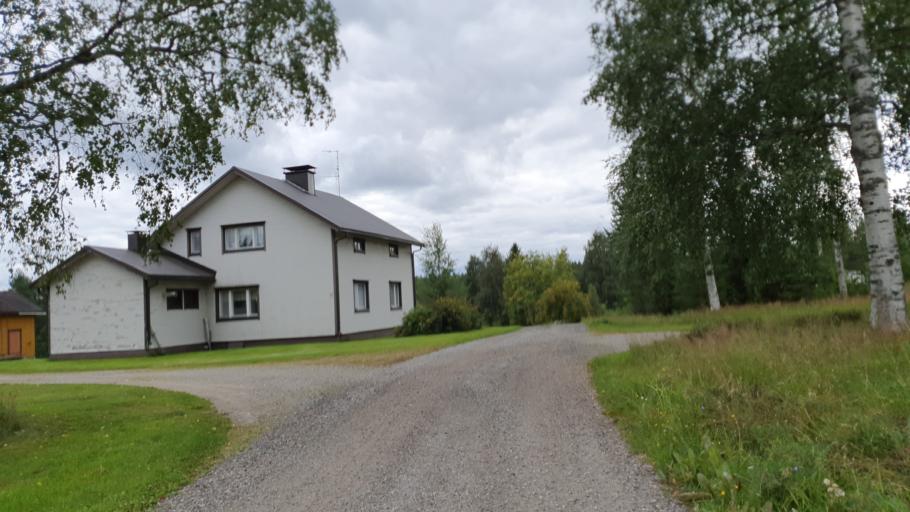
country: FI
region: Kainuu
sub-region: Kehys-Kainuu
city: Kuhmo
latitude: 64.1259
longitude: 29.4593
